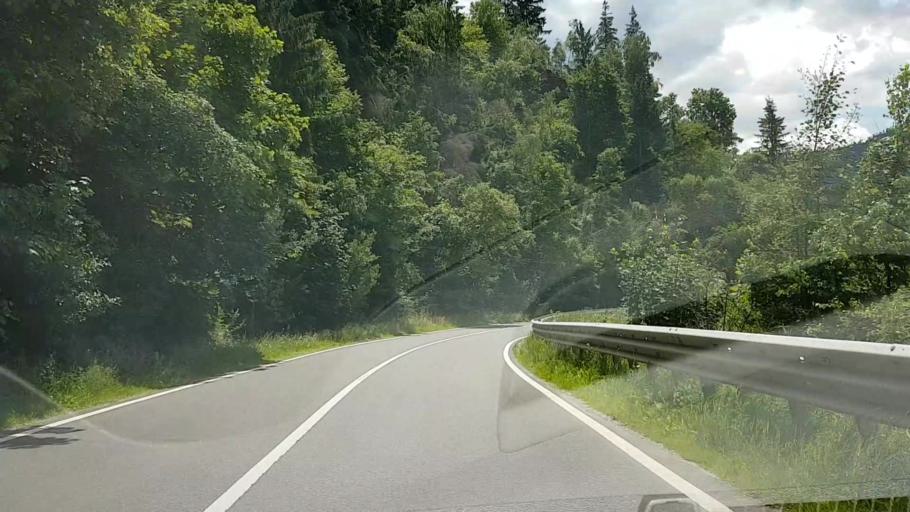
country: RO
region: Suceava
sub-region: Comuna Brosteni
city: Brosteni
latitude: 47.2528
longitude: 25.6962
